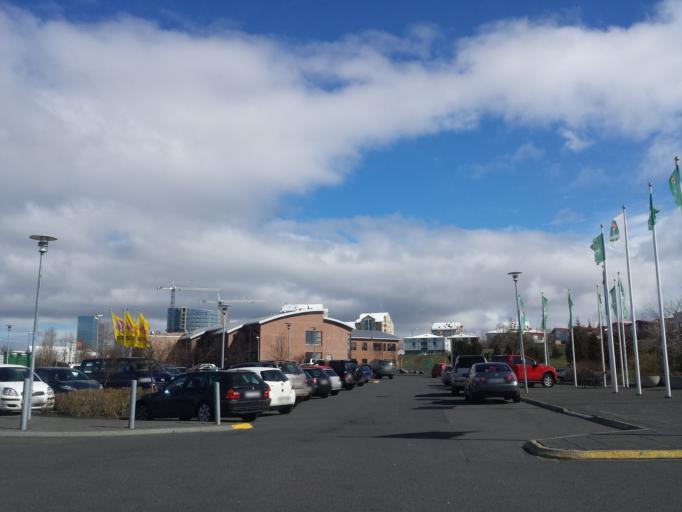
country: IS
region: Capital Region
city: Kopavogur
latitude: 64.1032
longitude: -21.8983
